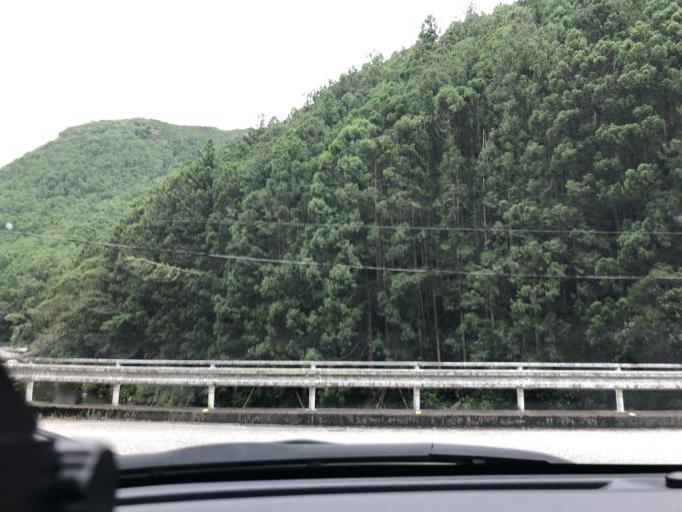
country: JP
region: Kochi
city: Kochi-shi
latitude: 33.6289
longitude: 133.5069
